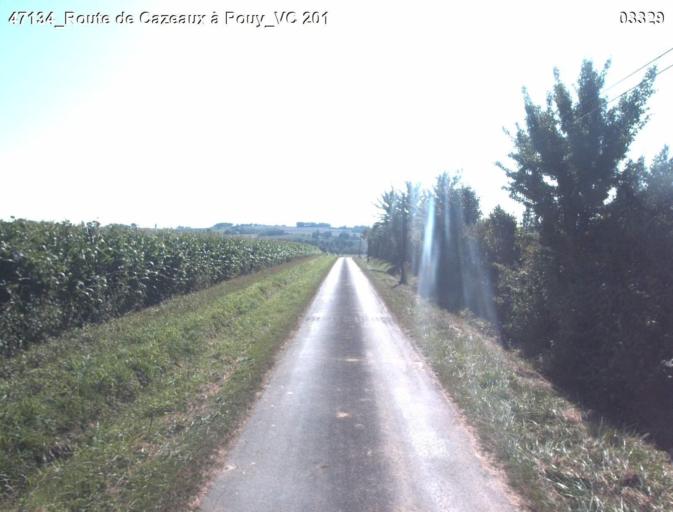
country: FR
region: Aquitaine
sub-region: Departement du Lot-et-Garonne
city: Mezin
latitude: 44.0282
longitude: 0.3083
